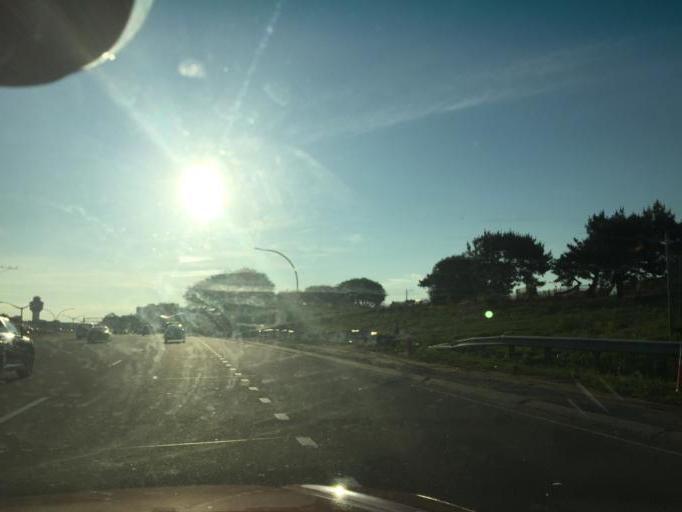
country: US
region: New York
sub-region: Queens County
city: Long Island City
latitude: 40.7671
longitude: -73.8863
